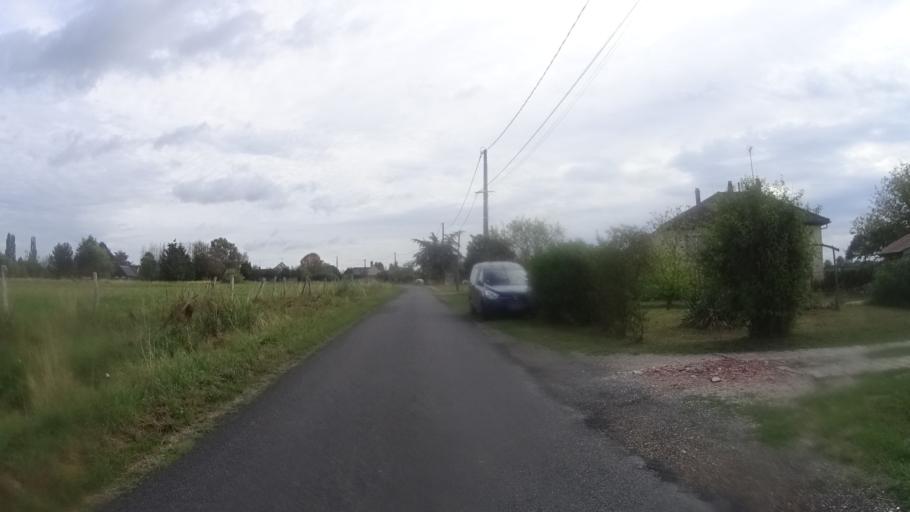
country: FR
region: Centre
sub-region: Departement du Loiret
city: Vitry-aux-Loges
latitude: 47.9882
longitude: 2.2075
